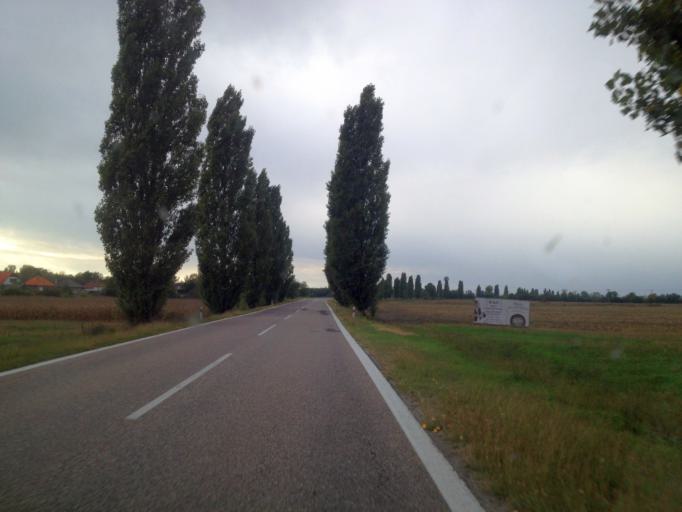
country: HU
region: Komarom-Esztergom
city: Labatlan
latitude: 47.7686
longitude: 18.4803
